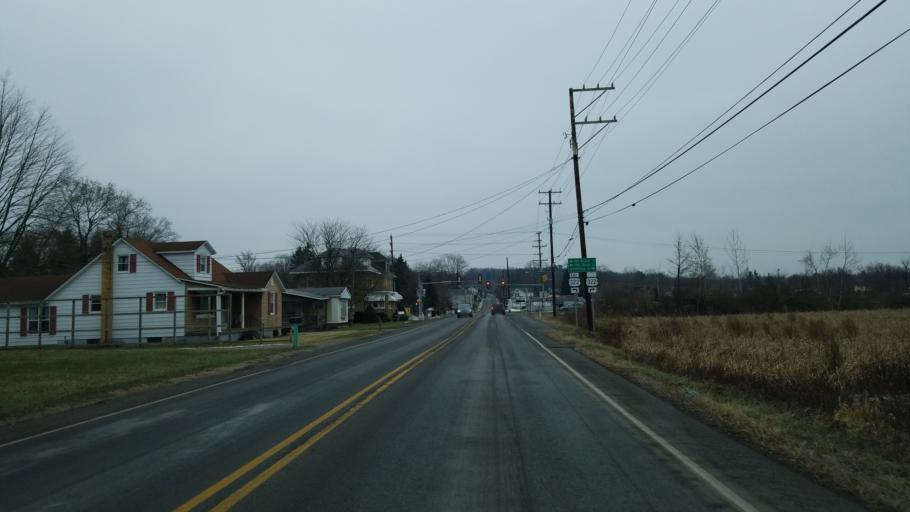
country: US
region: Pennsylvania
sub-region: Centre County
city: Philipsburg
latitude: 40.9061
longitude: -78.2215
